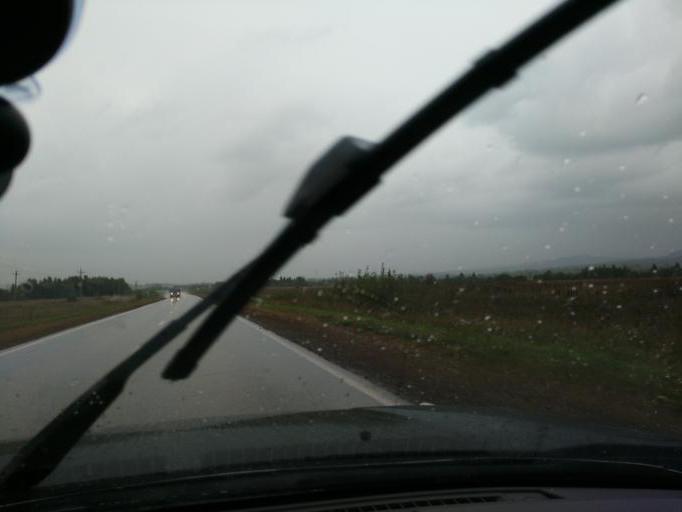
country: RU
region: Perm
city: Barda
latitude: 57.0761
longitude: 55.5426
